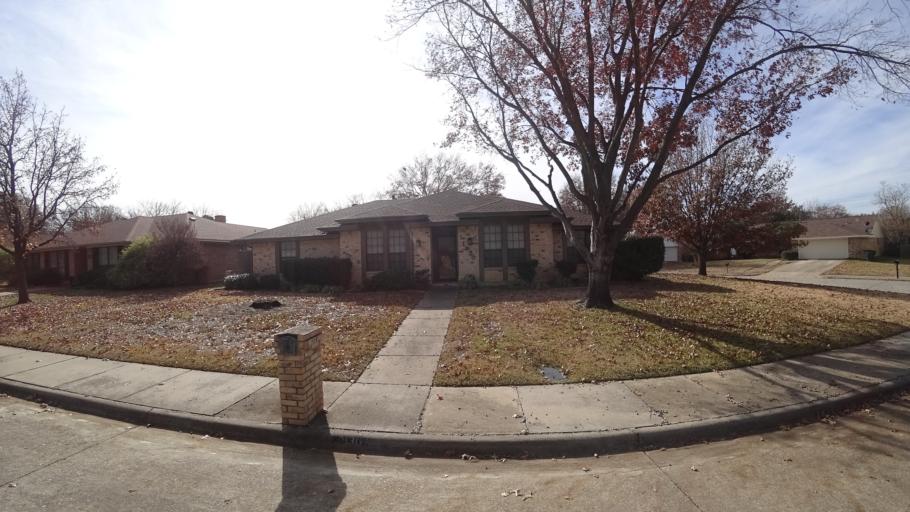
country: US
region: Texas
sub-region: Denton County
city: Highland Village
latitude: 33.0745
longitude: -97.0438
